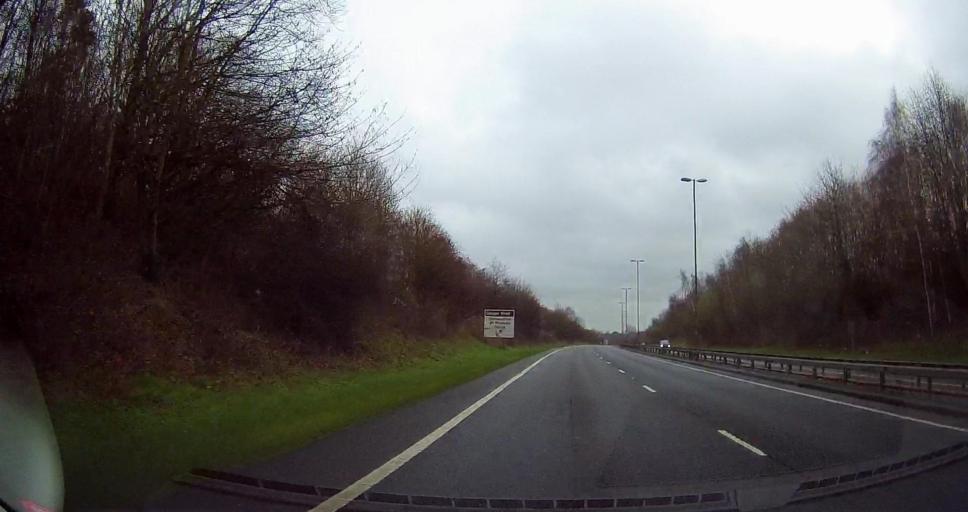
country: GB
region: England
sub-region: Kent
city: Strood
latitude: 51.4114
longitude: 0.4799
